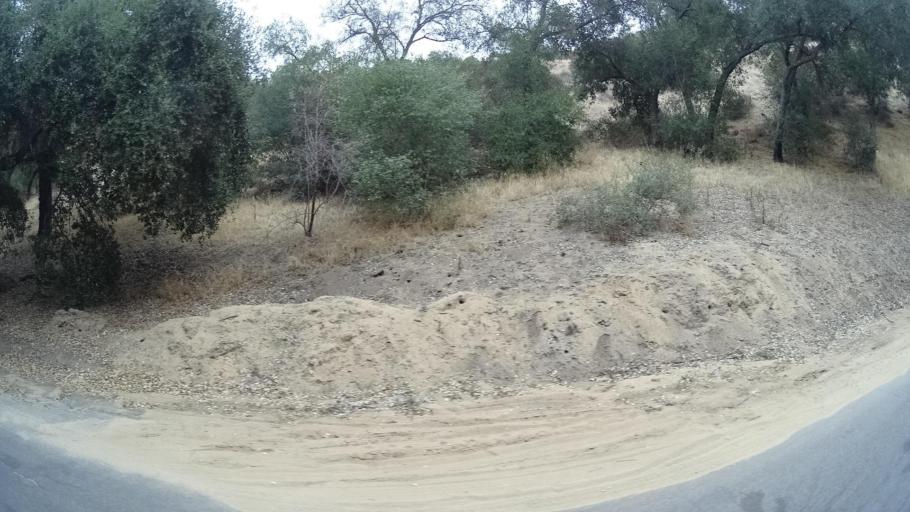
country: US
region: California
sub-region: San Diego County
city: Rainbow
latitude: 33.3768
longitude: -117.1622
